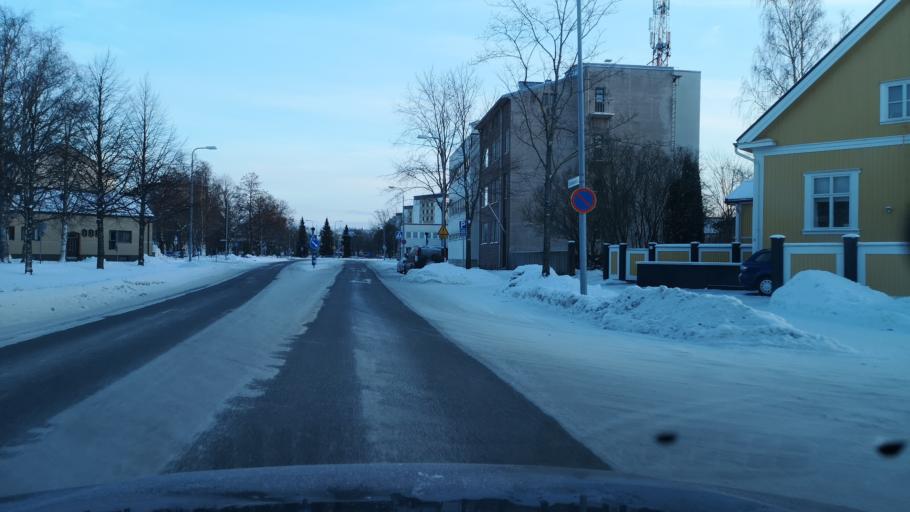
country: FI
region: Satakunta
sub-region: Pori
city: Pori
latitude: 61.4823
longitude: 21.7823
